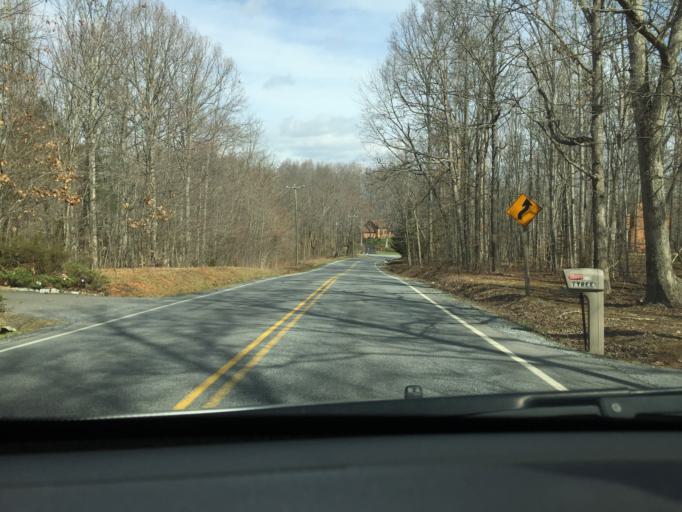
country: US
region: Virginia
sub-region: Bedford County
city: Forest
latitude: 37.3209
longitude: -79.3100
